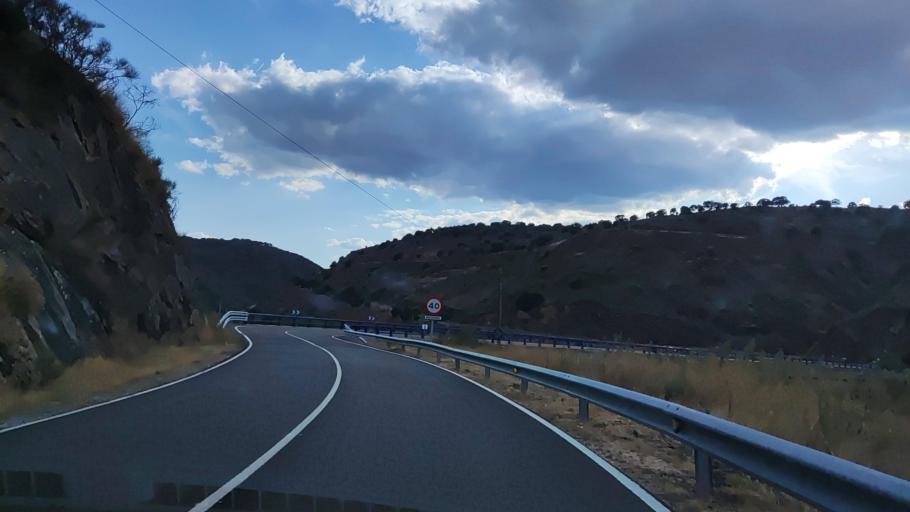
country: ES
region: Castille and Leon
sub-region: Provincia de Salamanca
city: Pastores
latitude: 40.4976
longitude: -6.4951
